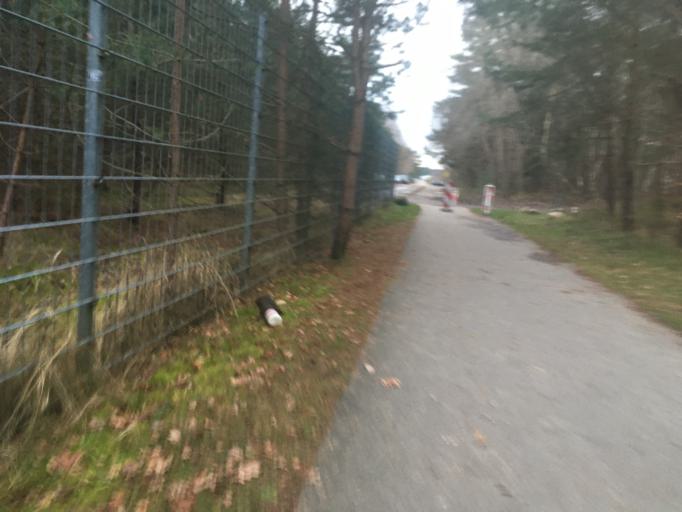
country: DE
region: Mecklenburg-Vorpommern
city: Sagard
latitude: 54.4581
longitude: 13.5671
